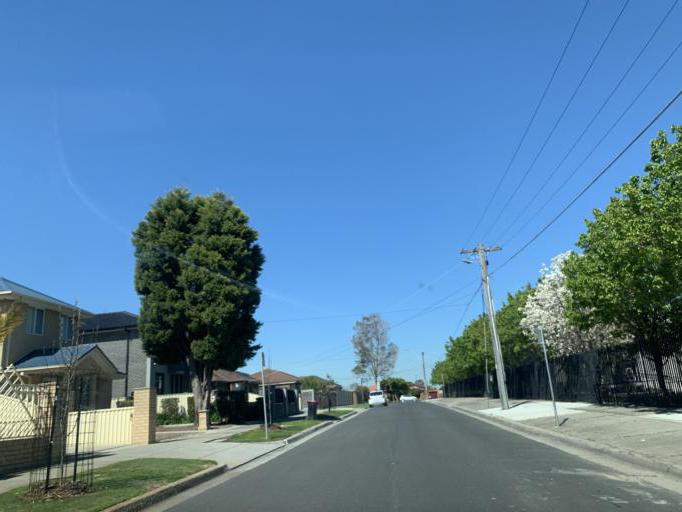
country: AU
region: Victoria
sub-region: Greater Dandenong
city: Dandenong
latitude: -37.9981
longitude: 145.2125
